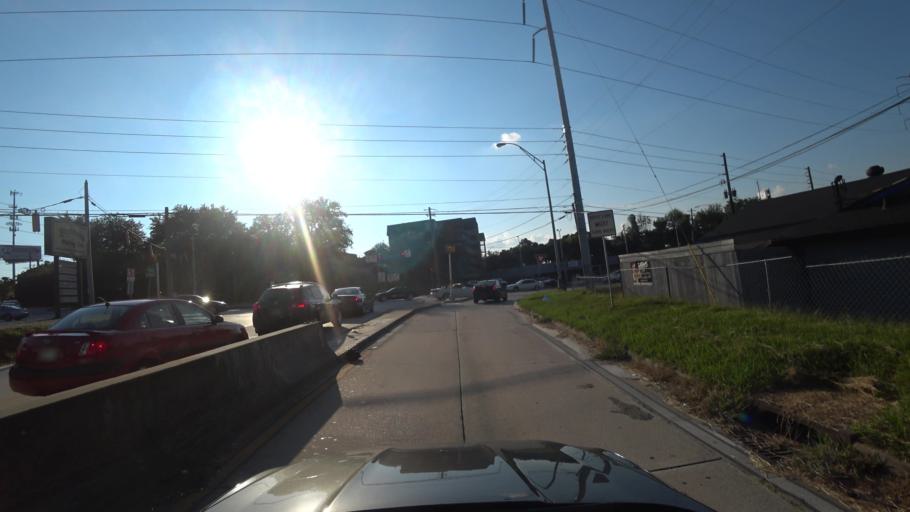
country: US
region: Georgia
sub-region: DeKalb County
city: Druid Hills
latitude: 33.8116
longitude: -84.3664
